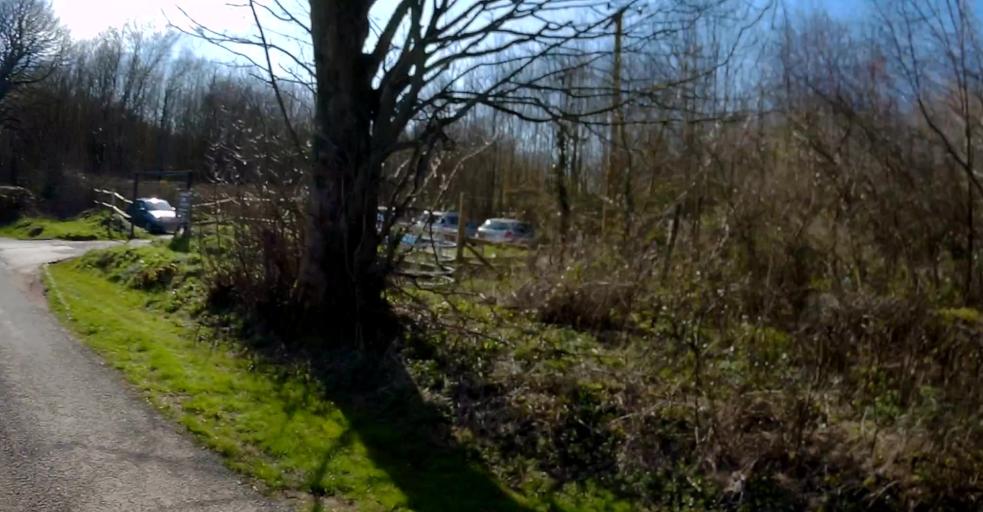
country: GB
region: England
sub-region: Hampshire
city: Four Marks
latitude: 51.1703
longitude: -1.0641
